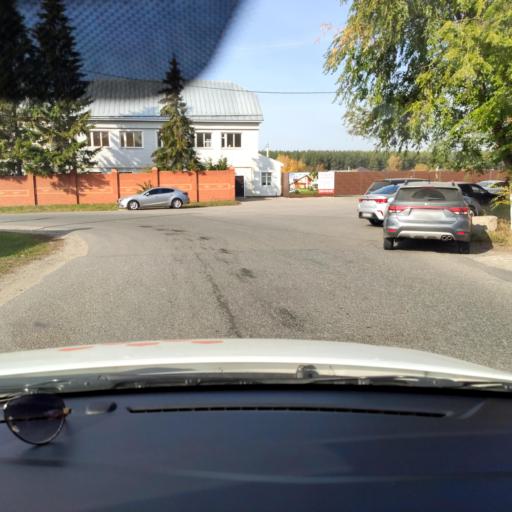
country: RU
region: Tatarstan
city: Stolbishchi
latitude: 55.6783
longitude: 49.1217
